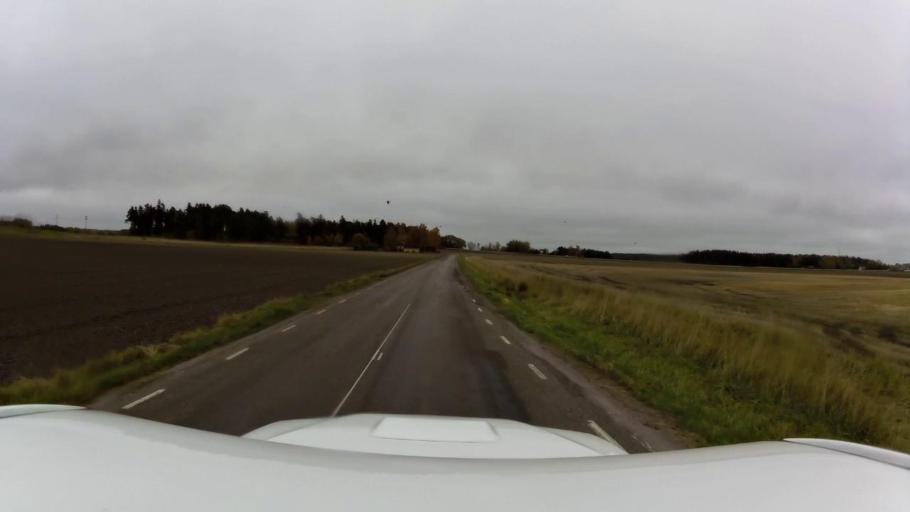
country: SE
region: OEstergoetland
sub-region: Linkopings Kommun
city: Linghem
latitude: 58.4348
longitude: 15.7172
